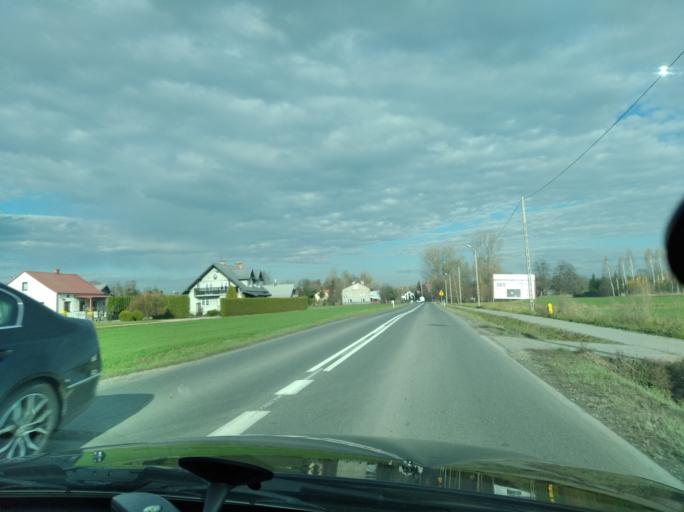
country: PL
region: Subcarpathian Voivodeship
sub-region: Powiat ropczycko-sedziszowski
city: Ostrow
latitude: 50.0932
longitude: 21.5930
